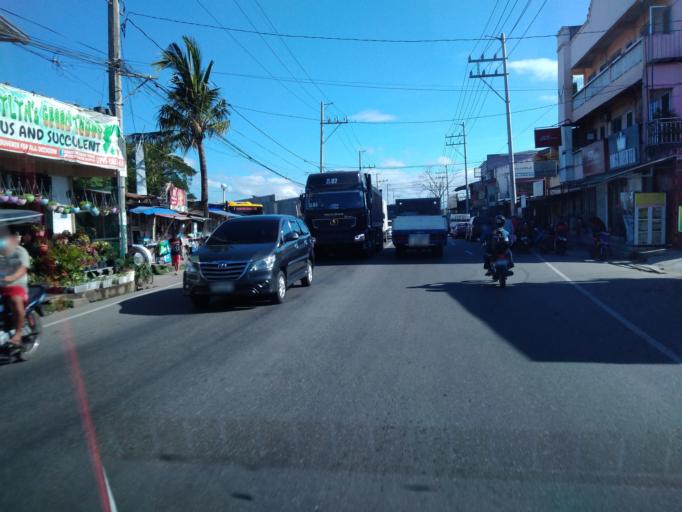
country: PH
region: Central Luzon
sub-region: Province of Bulacan
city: Santa Maria
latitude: 14.8244
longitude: 120.9550
